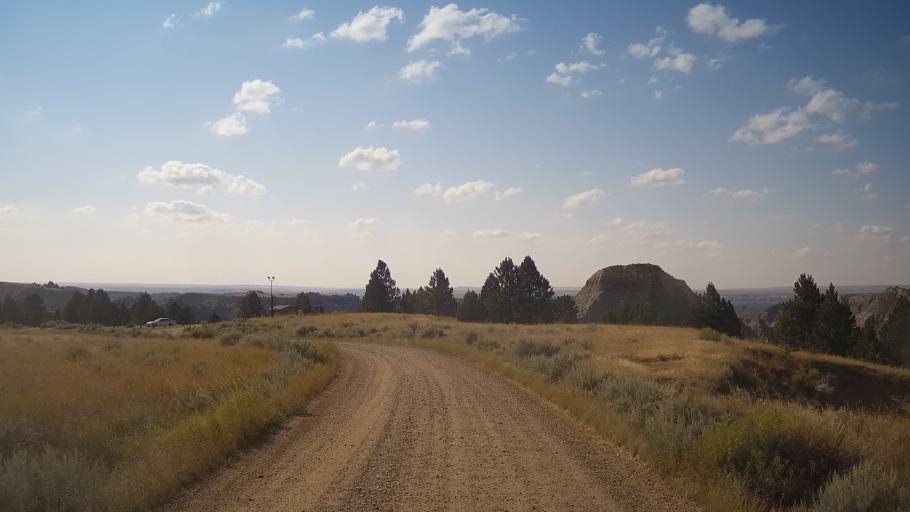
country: US
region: Montana
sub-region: Dawson County
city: Glendive
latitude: 47.0627
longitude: -104.6715
